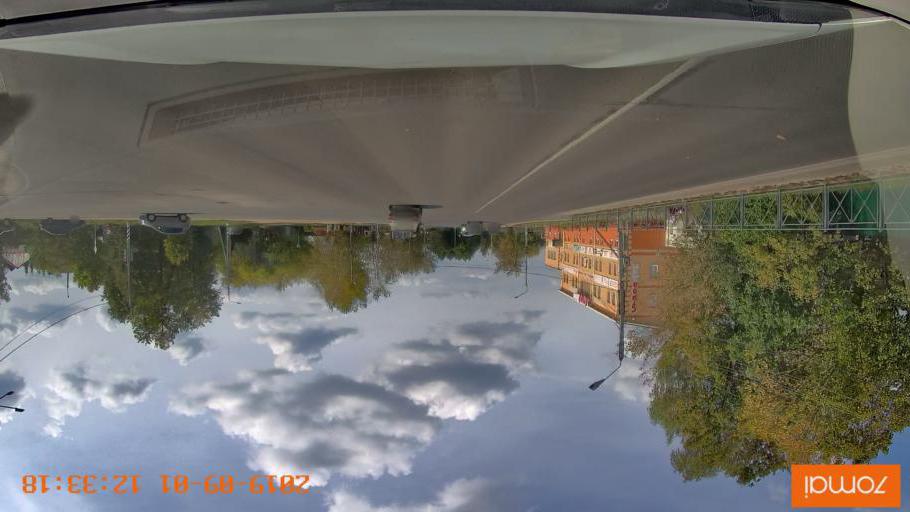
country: RU
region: Kaluga
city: Maloyaroslavets
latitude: 55.0059
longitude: 36.4451
